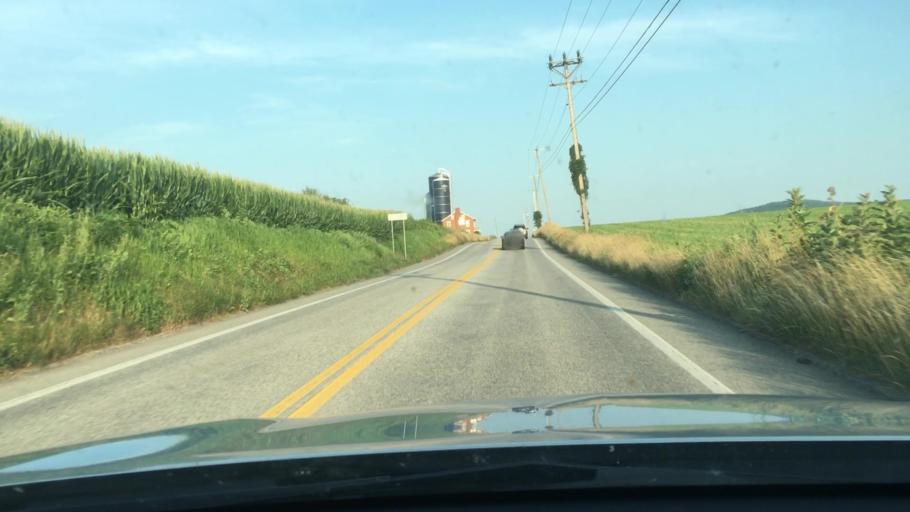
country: US
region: Pennsylvania
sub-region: Cumberland County
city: Boiling Springs
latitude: 40.1596
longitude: -77.0925
